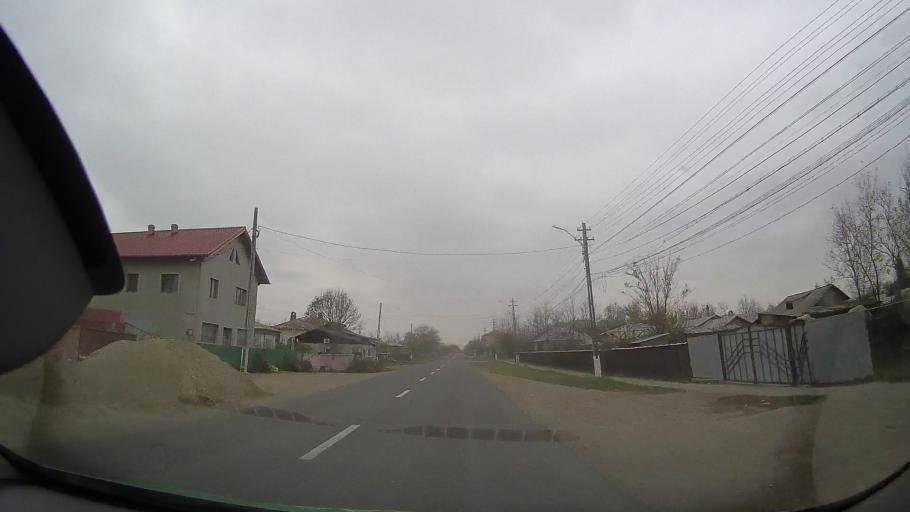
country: RO
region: Ialomita
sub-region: Comuna Garbovi
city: Garbovi
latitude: 44.7842
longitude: 26.7664
